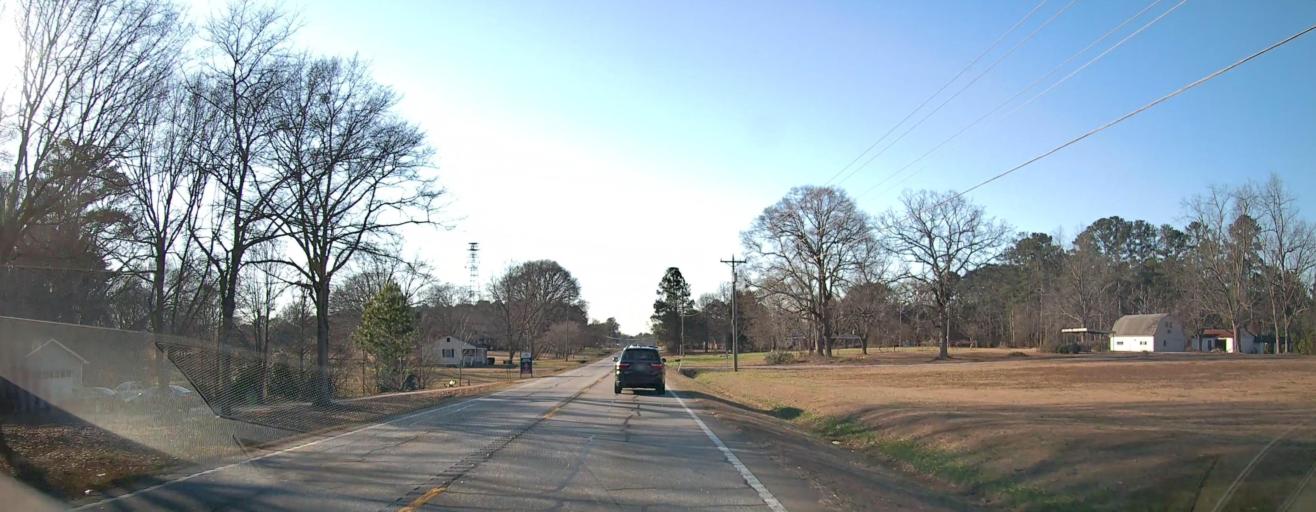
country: US
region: Georgia
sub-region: Henry County
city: Hampton
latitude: 33.4236
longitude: -84.2742
